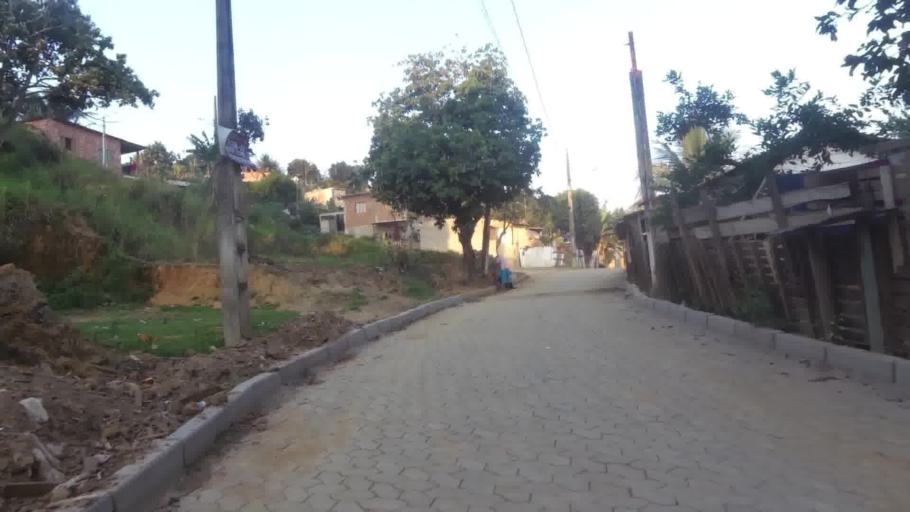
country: BR
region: Espirito Santo
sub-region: Piuma
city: Piuma
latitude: -20.8283
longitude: -40.7222
